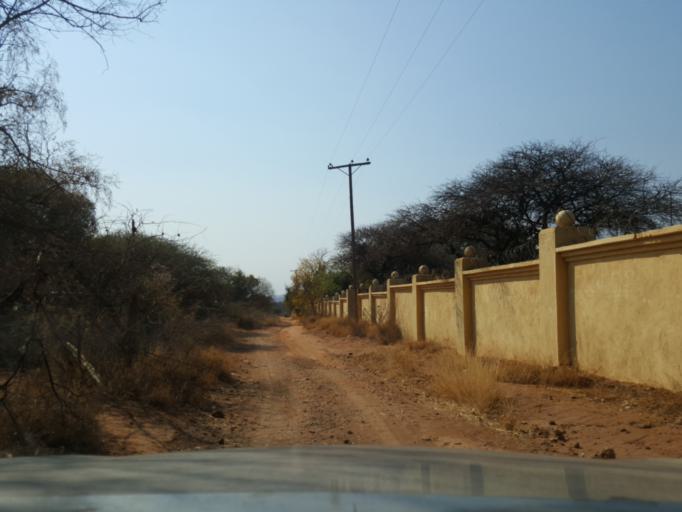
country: BW
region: South East
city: Lobatse
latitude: -25.1768
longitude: 25.6814
